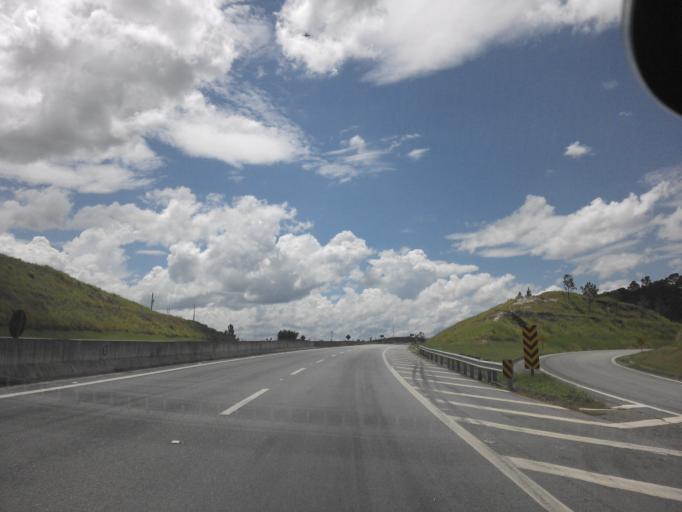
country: BR
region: Sao Paulo
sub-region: Jacarei
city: Jacarei
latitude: -23.3135
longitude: -46.0457
